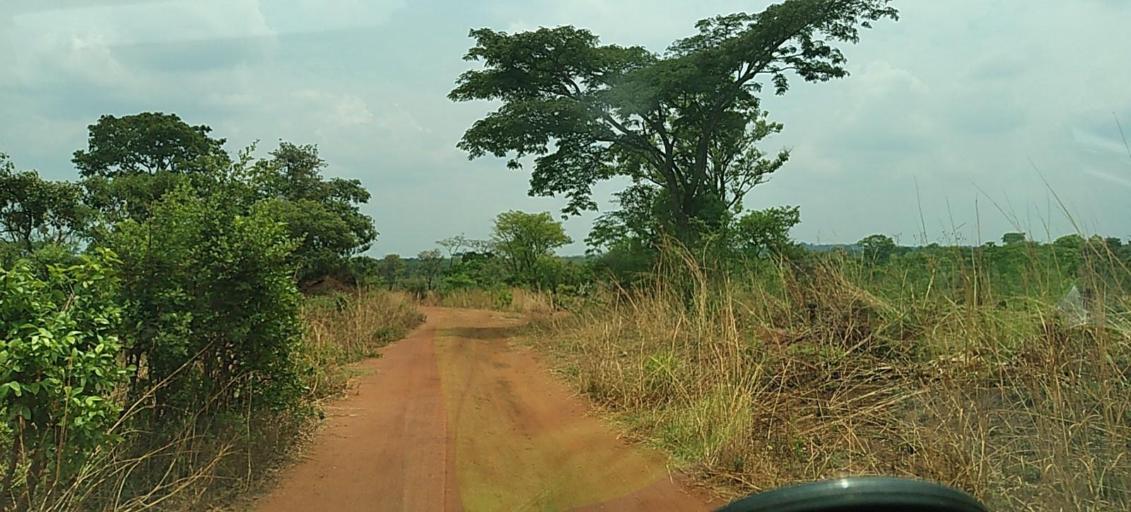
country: ZM
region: North-Western
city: Kansanshi
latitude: -12.0481
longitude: 26.3702
